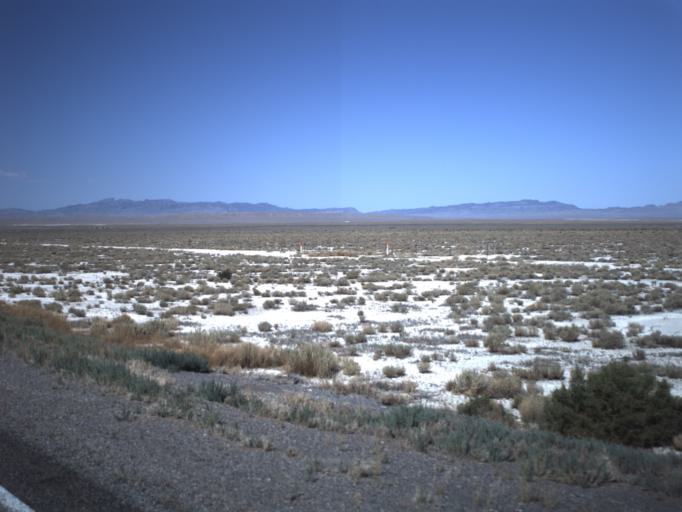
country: US
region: Utah
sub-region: Millard County
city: Delta
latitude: 39.2378
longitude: -112.9190
